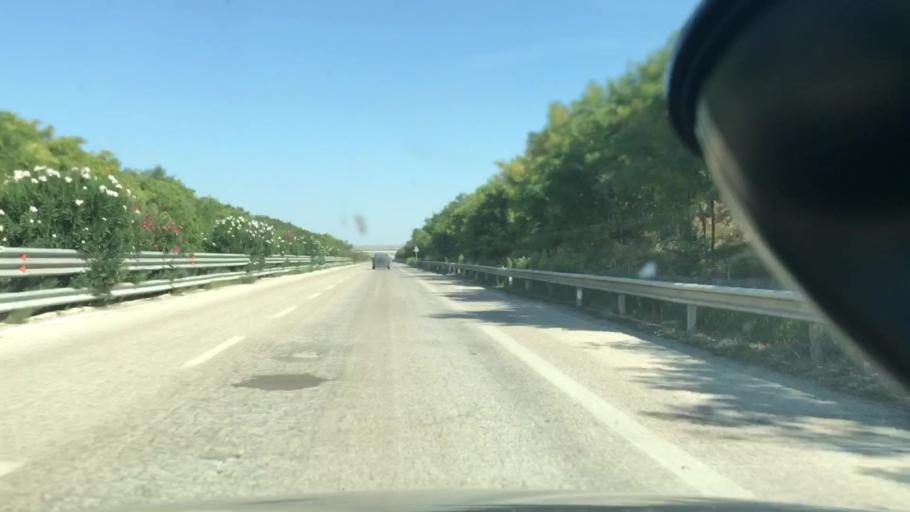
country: IT
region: Apulia
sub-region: Provincia di Foggia
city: Ordona
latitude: 41.2847
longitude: 15.5540
